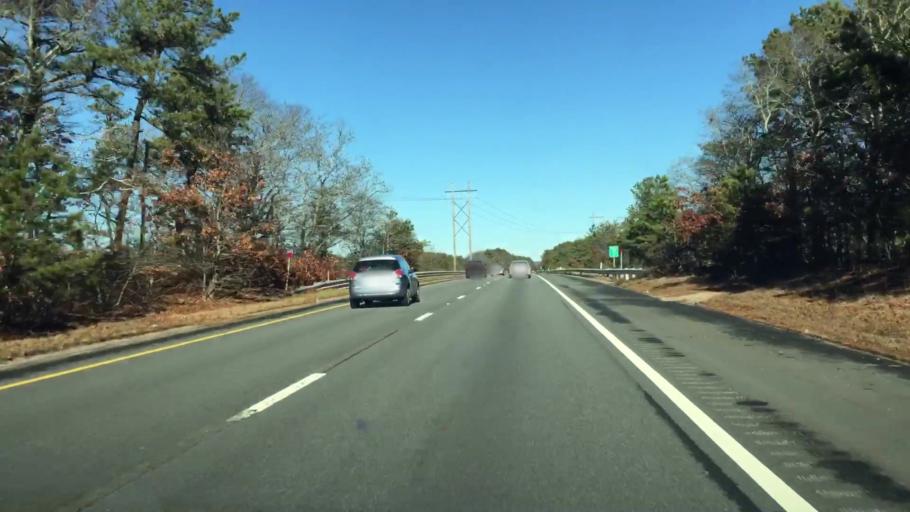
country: US
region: Massachusetts
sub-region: Barnstable County
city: Pocasset
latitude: 41.6658
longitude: -70.5991
